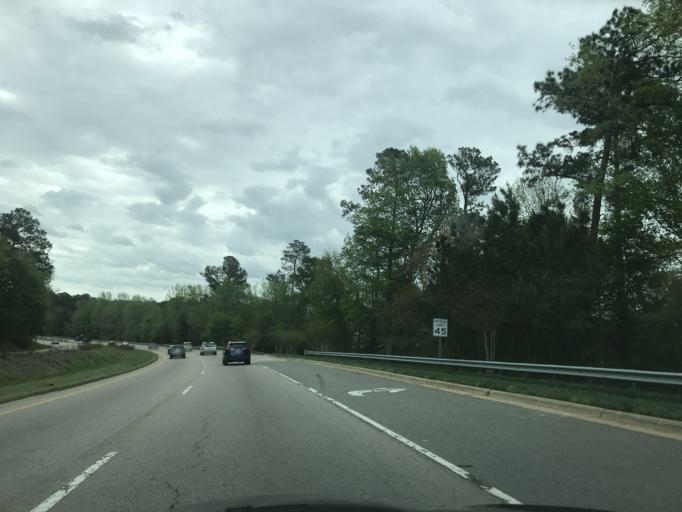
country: US
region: North Carolina
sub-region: Wake County
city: Knightdale
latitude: 35.7921
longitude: -78.5447
